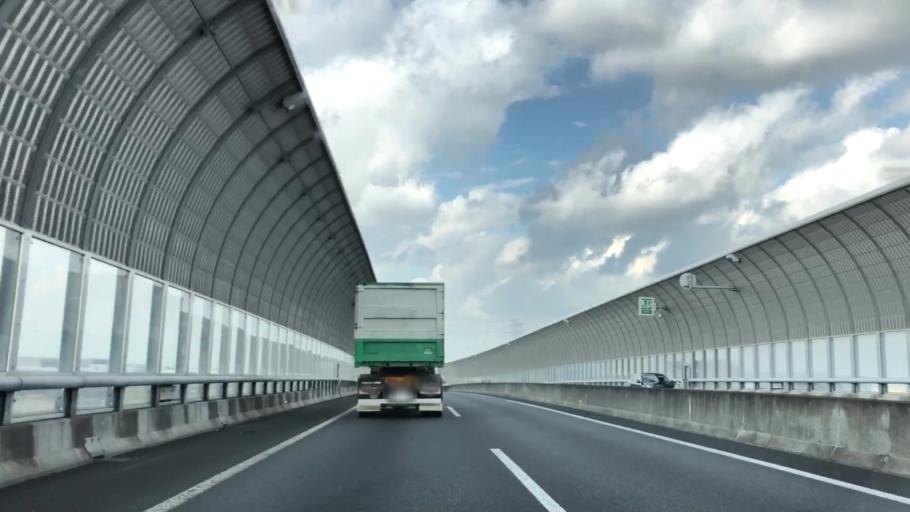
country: JP
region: Saitama
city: Yashio-shi
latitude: 35.8182
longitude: 139.8742
